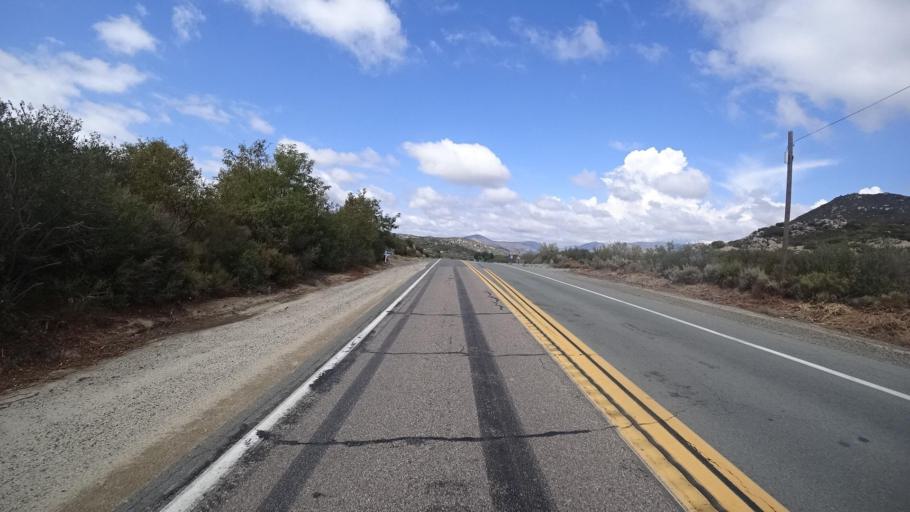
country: US
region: California
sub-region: San Diego County
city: Campo
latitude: 32.6883
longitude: -116.4886
